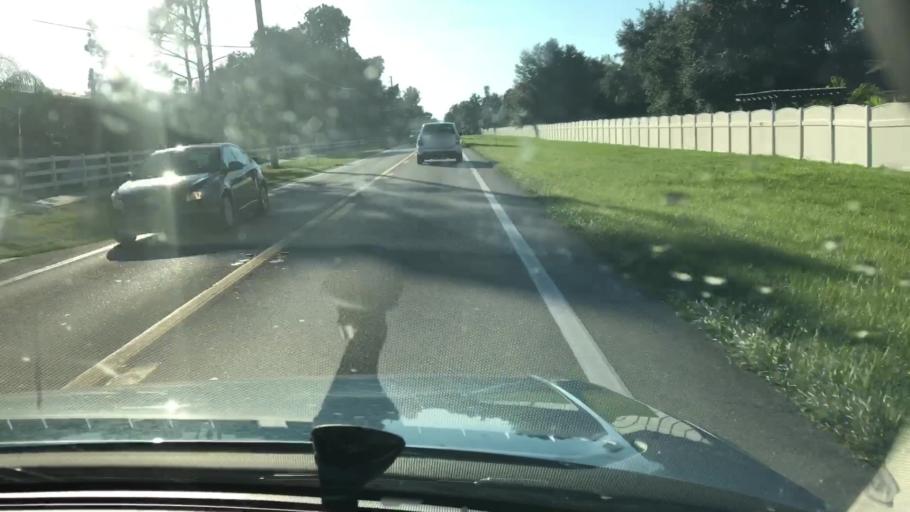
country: US
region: Florida
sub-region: Polk County
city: Gibsonia
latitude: 28.1356
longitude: -81.9914
